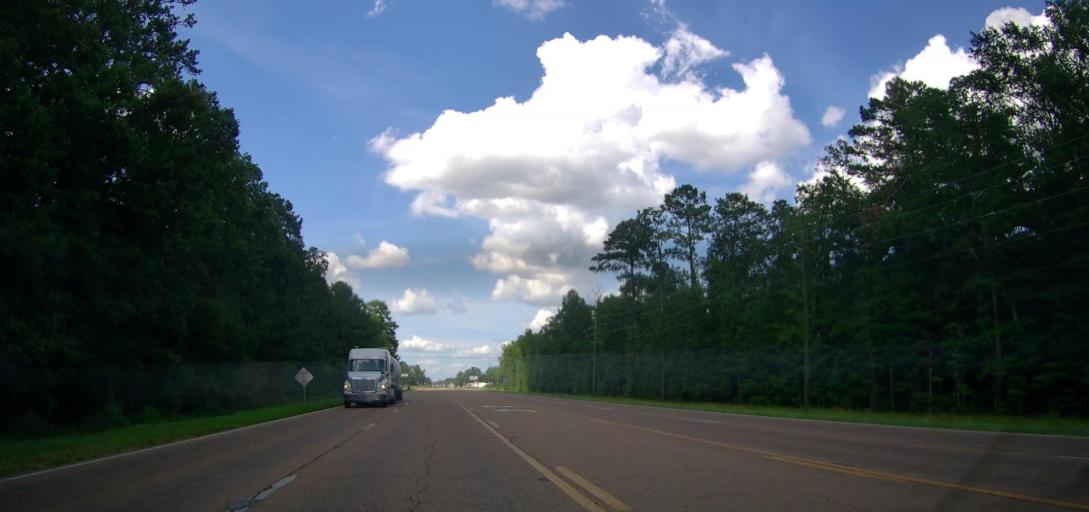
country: US
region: Mississippi
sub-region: Lowndes County
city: Columbus Air Force Base
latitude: 33.5836
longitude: -88.4279
